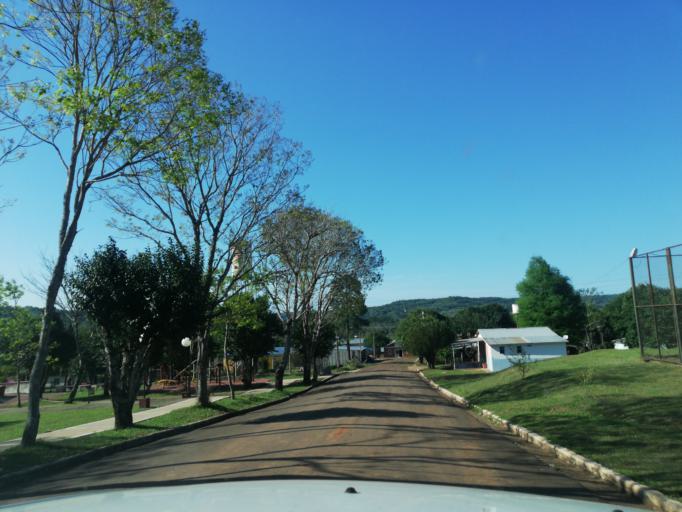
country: AR
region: Misiones
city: Arroyo del Medio
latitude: -27.6986
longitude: -55.4045
